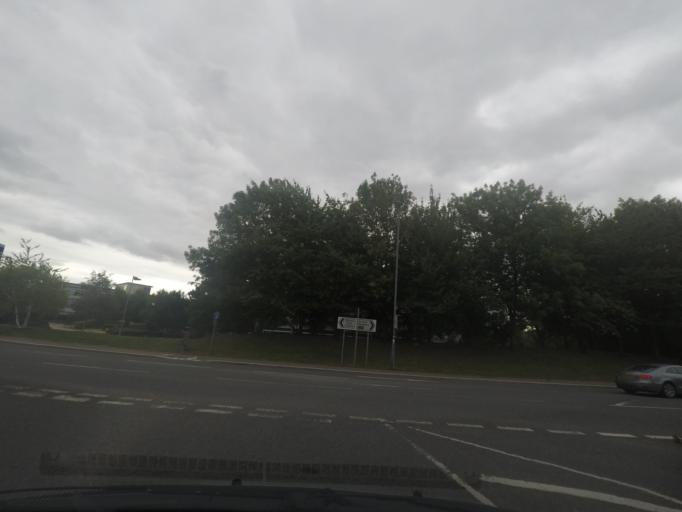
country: GB
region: England
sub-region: Oxfordshire
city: Harwell
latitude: 51.6224
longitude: -1.3026
